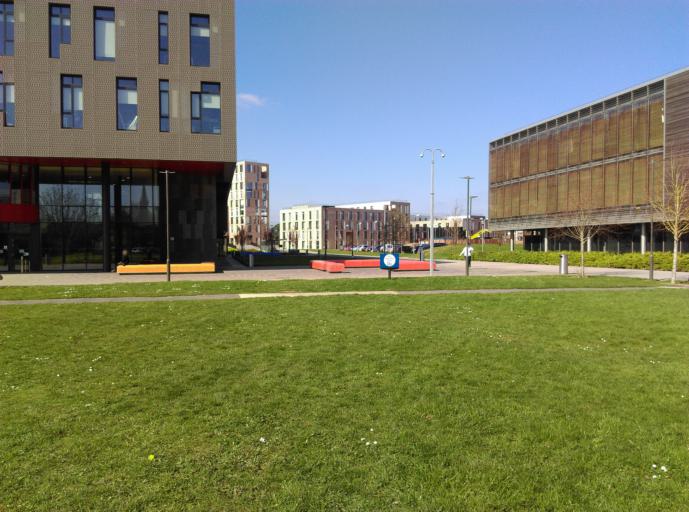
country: IE
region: Leinster
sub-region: Kildare
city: Maynooth
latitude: 53.3844
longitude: -6.6011
